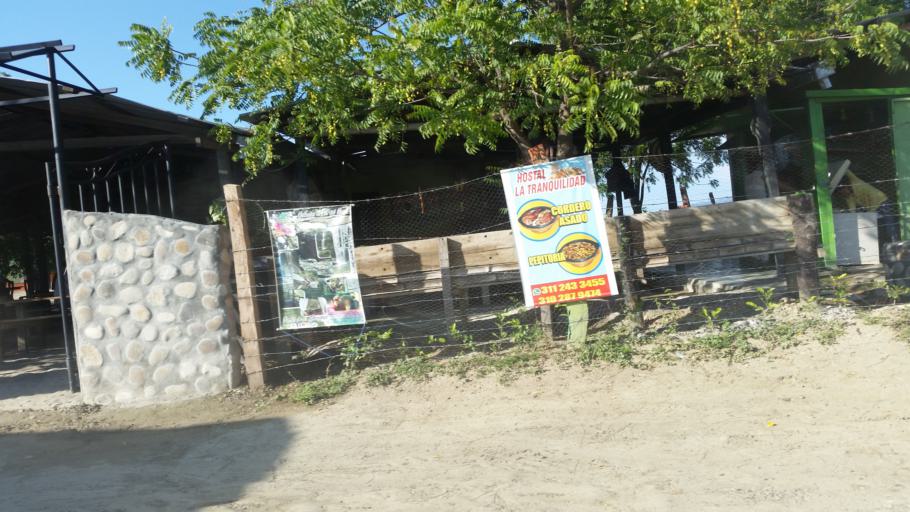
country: CO
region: Huila
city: Villavieja
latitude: 3.2331
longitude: -75.1588
